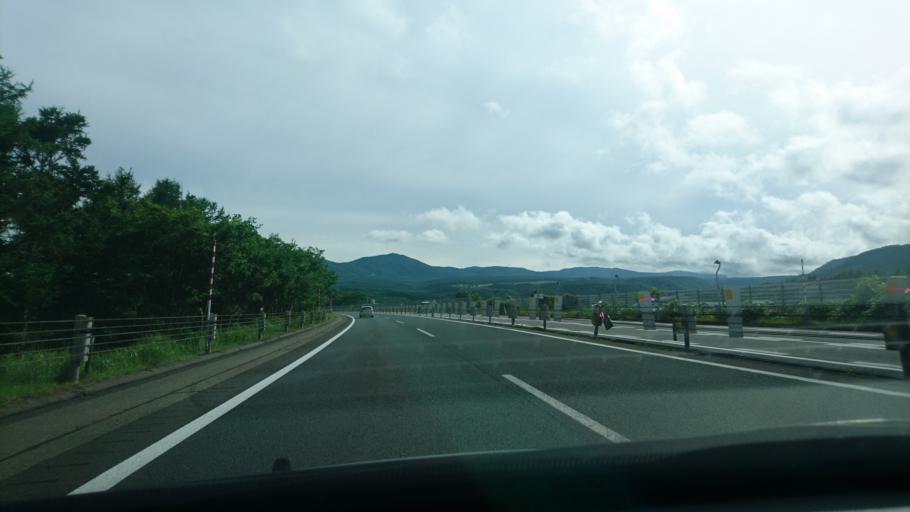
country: JP
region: Akita
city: Hanawa
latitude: 40.0316
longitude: 140.9847
